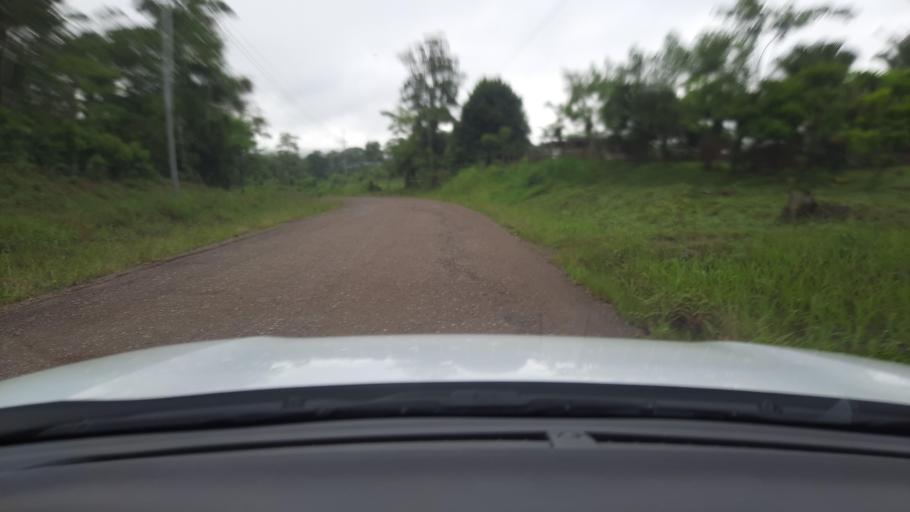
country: CR
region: Alajuela
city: San Jose
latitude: 11.0024
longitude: -85.3077
